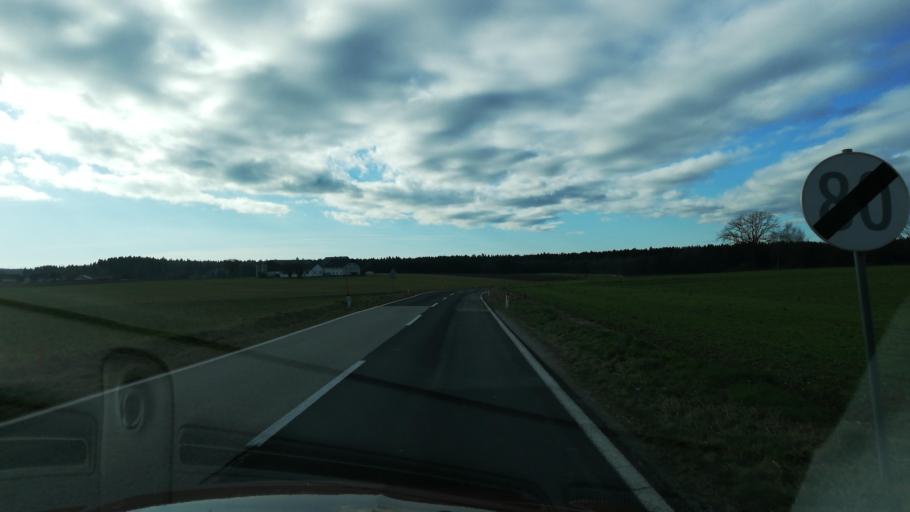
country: AT
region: Upper Austria
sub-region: Politischer Bezirk Braunau am Inn
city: Braunau am Inn
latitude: 48.1971
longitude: 13.0870
